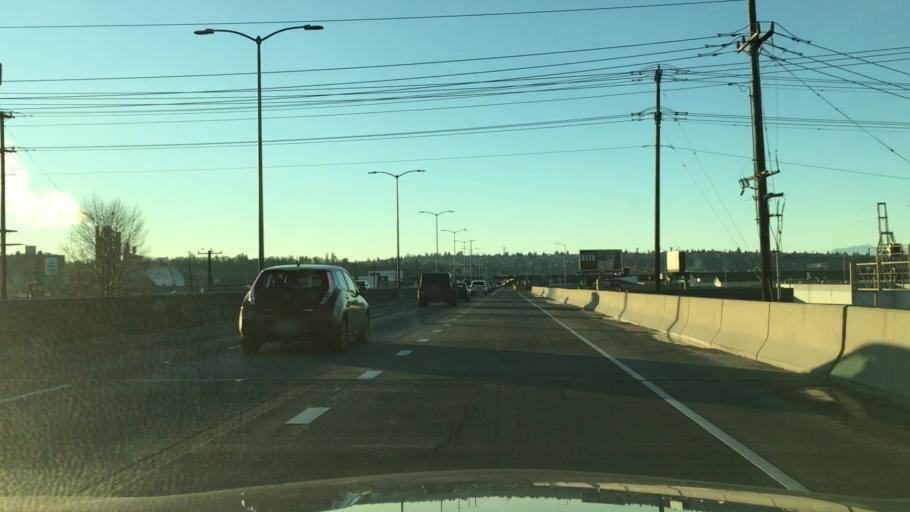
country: US
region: Washington
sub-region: King County
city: Seattle
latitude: 47.5717
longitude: -122.3309
